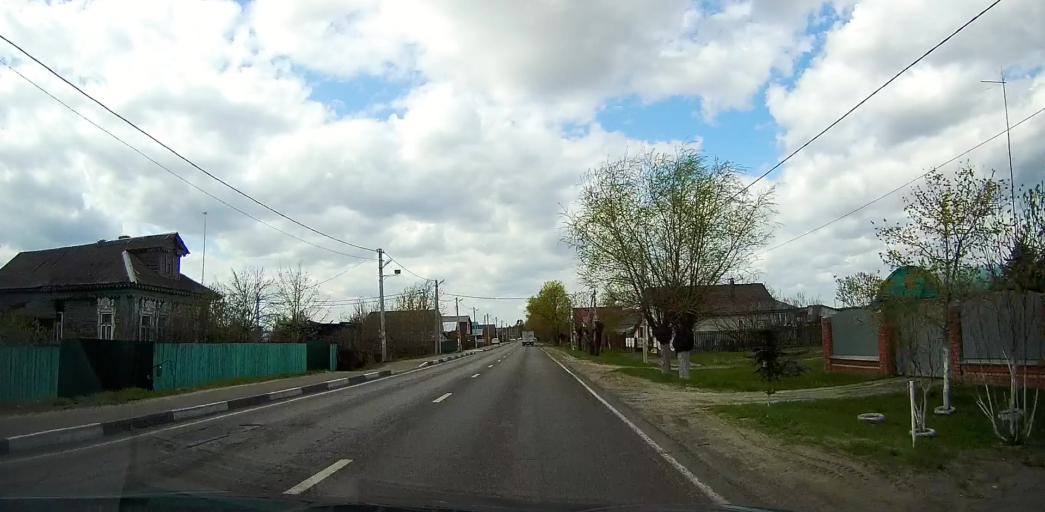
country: RU
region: Moskovskaya
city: Davydovo
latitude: 55.6383
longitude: 38.8655
